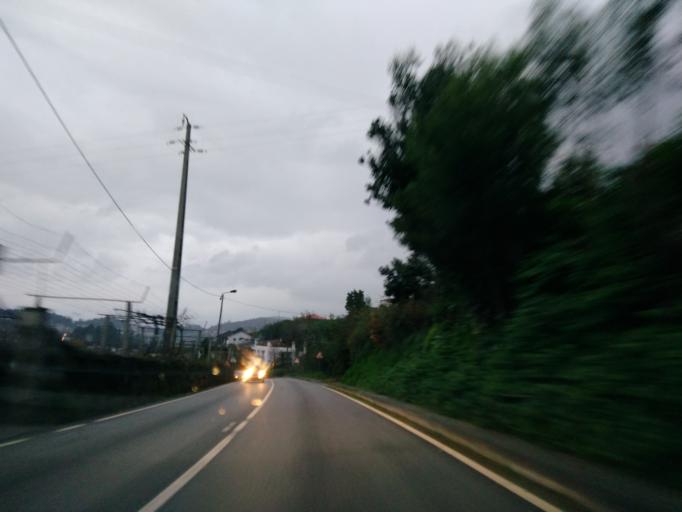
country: PT
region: Braga
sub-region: Braga
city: Oliveira
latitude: 41.4656
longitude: -8.4902
